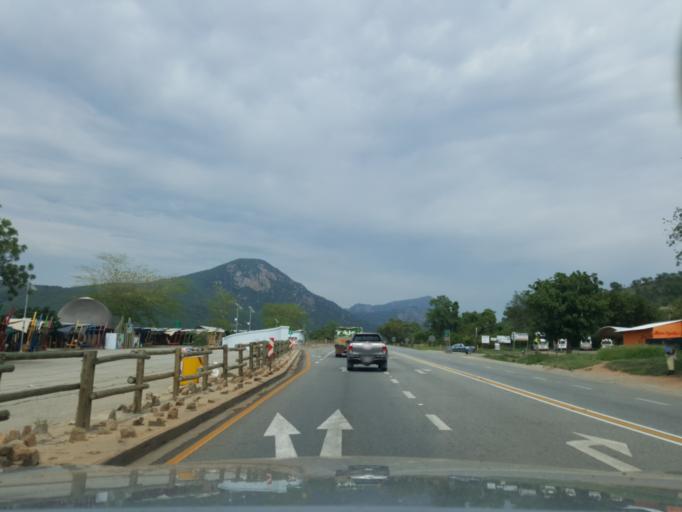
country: SZ
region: Hhohho
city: Ntfonjeni
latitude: -25.5369
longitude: 31.3029
